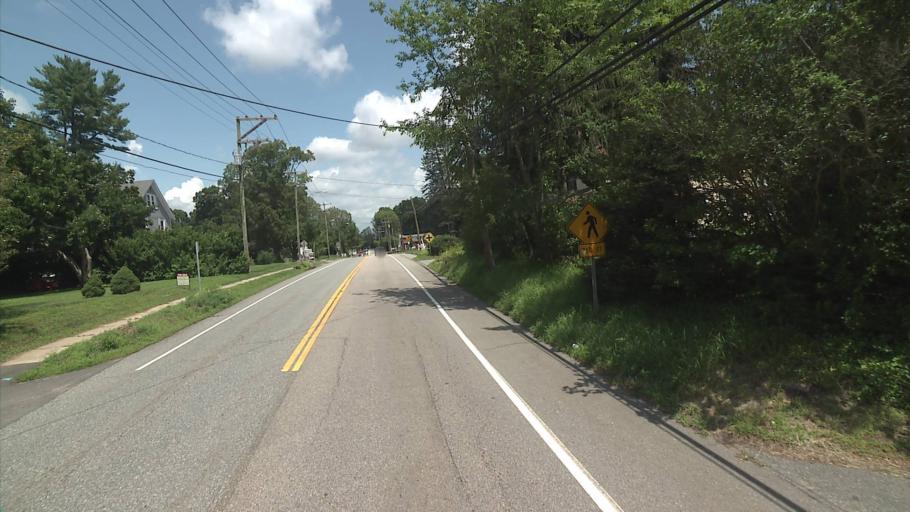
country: US
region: Connecticut
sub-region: Middlesex County
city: Chester Center
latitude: 41.4002
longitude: -72.4416
